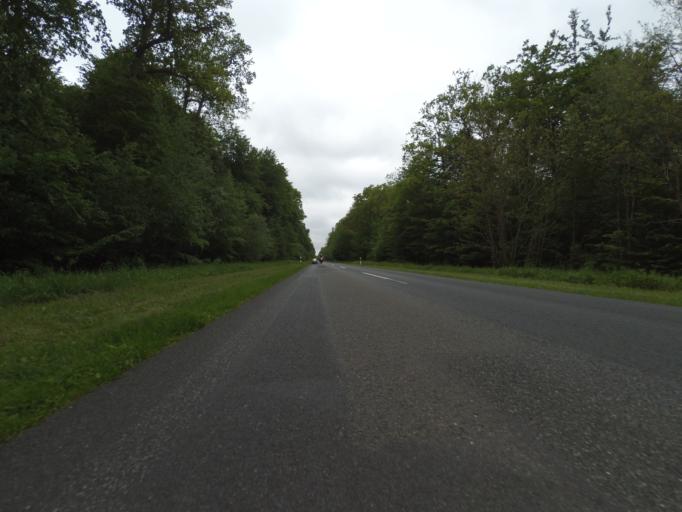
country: DE
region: Lower Saxony
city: Ribbesbuttel
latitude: 52.4063
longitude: 10.4942
